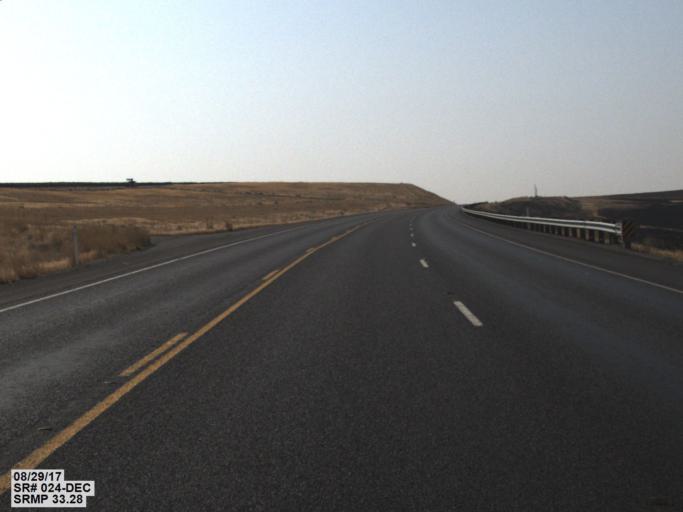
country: US
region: Washington
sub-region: Grant County
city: Desert Aire
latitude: 46.5500
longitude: -119.8263
